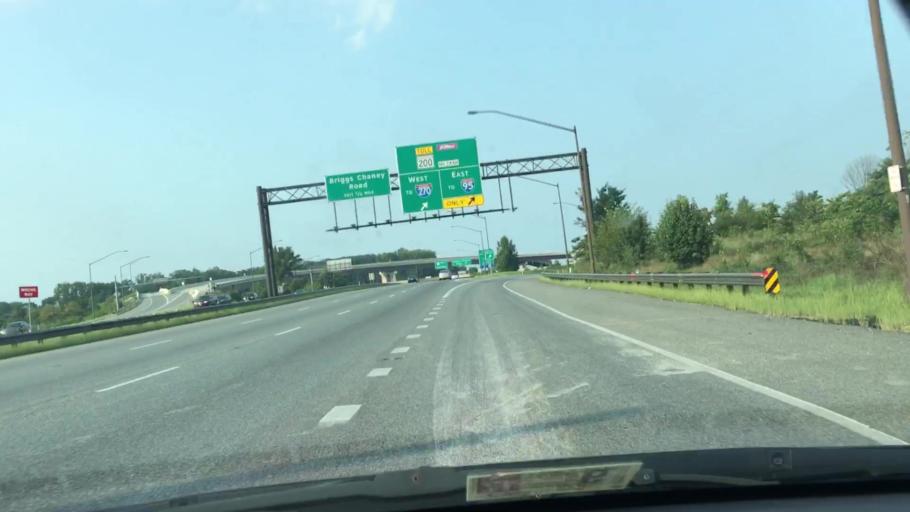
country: US
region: Maryland
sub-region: Montgomery County
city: Fairland
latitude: 39.0735
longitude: -76.9554
